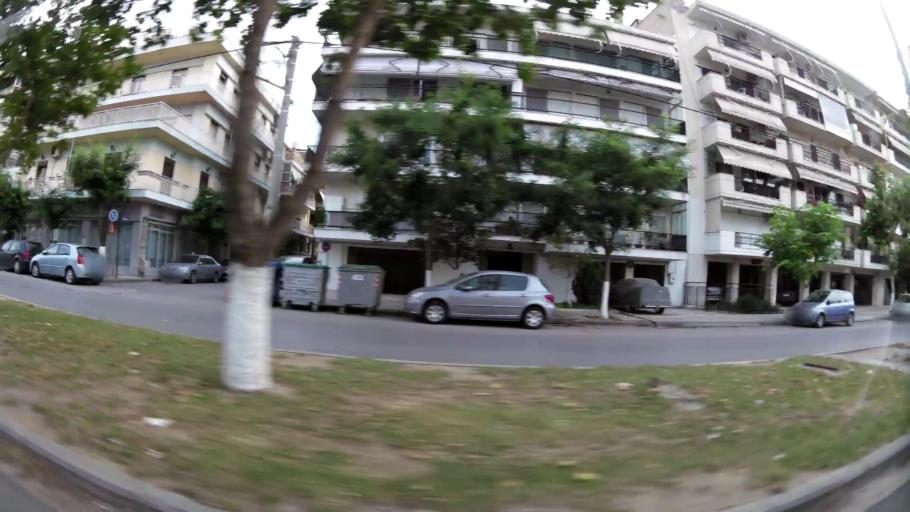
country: GR
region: Central Macedonia
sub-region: Nomos Thessalonikis
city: Ampelokipoi
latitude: 40.6590
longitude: 22.9243
